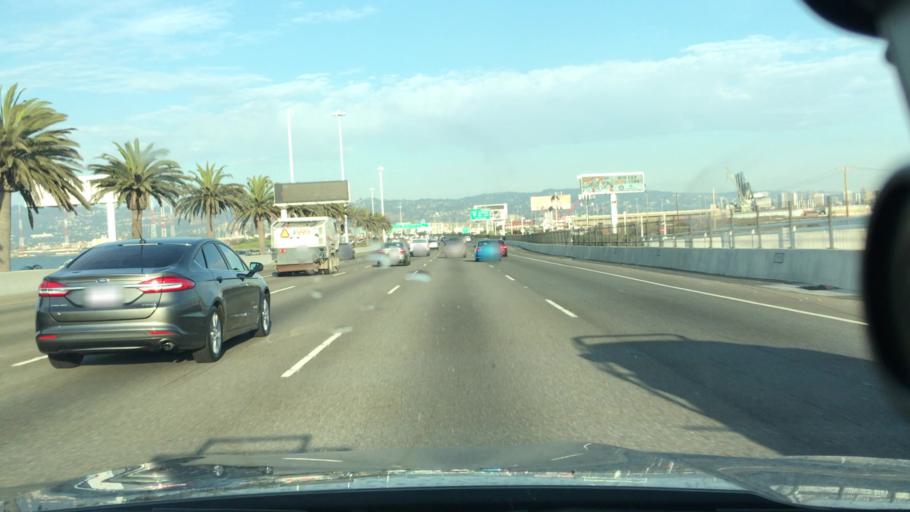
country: US
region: California
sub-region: Alameda County
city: Emeryville
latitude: 37.8201
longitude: -122.3260
